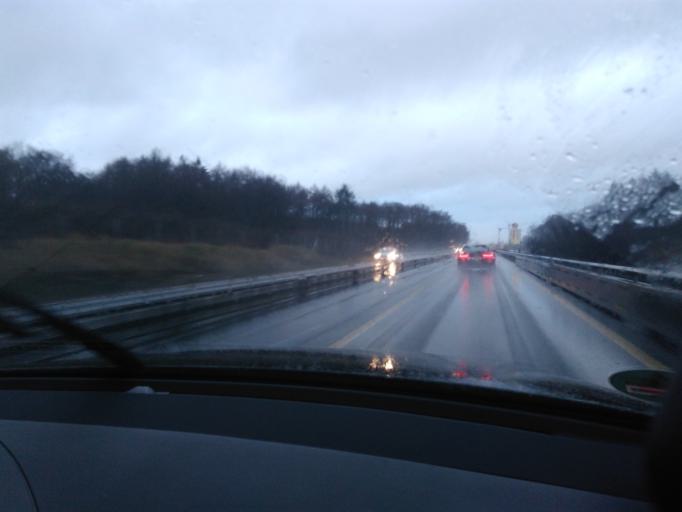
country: DE
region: Schleswig-Holstein
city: Bimohlen
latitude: 53.9302
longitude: 9.9429
